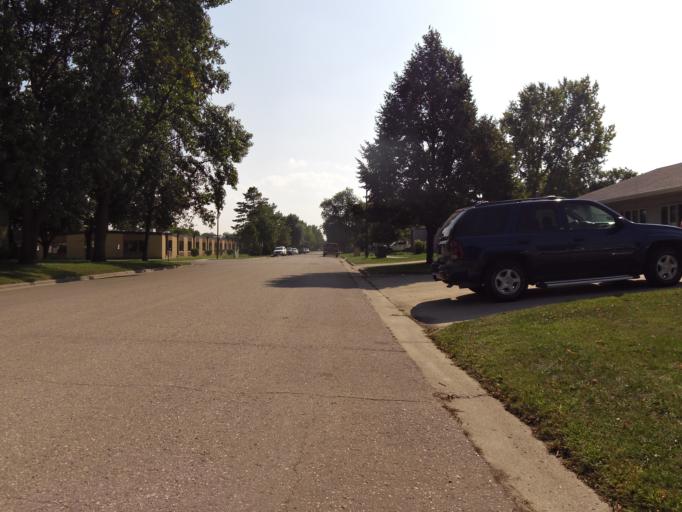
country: US
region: North Dakota
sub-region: Walsh County
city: Grafton
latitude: 48.4219
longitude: -97.4011
